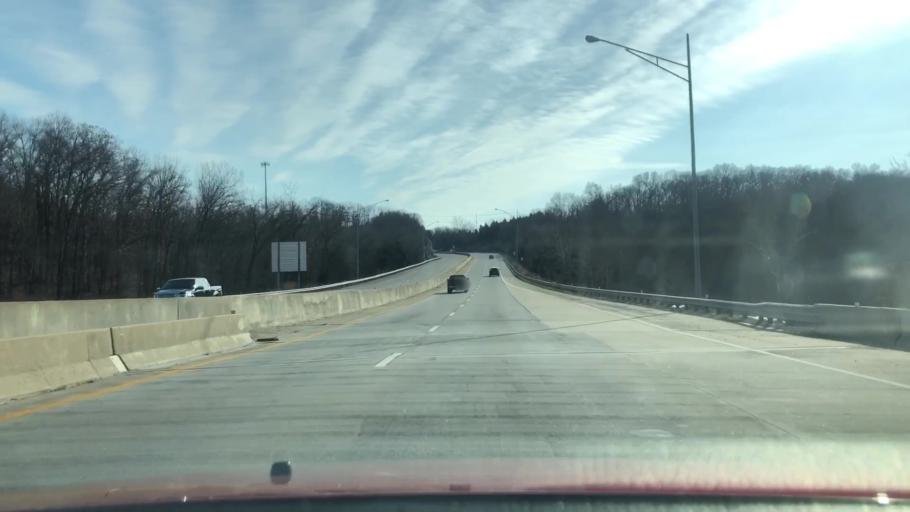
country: US
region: Missouri
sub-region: Christian County
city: Ozark
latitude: 37.1242
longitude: -93.2259
